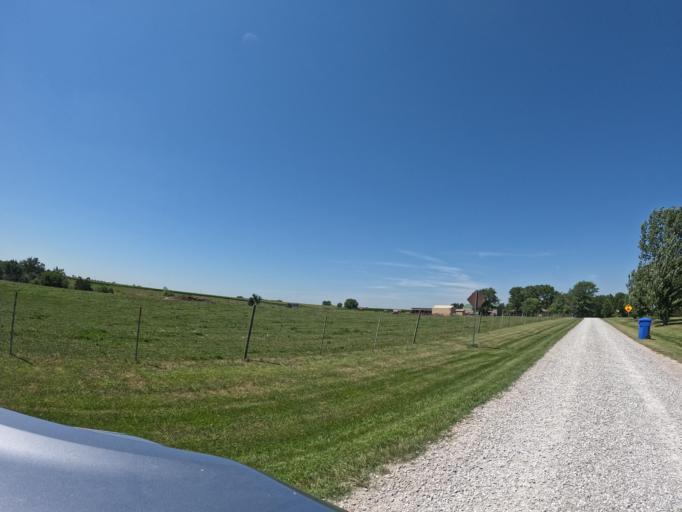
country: US
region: Iowa
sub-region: Monroe County
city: Albia
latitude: 41.0268
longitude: -92.7712
